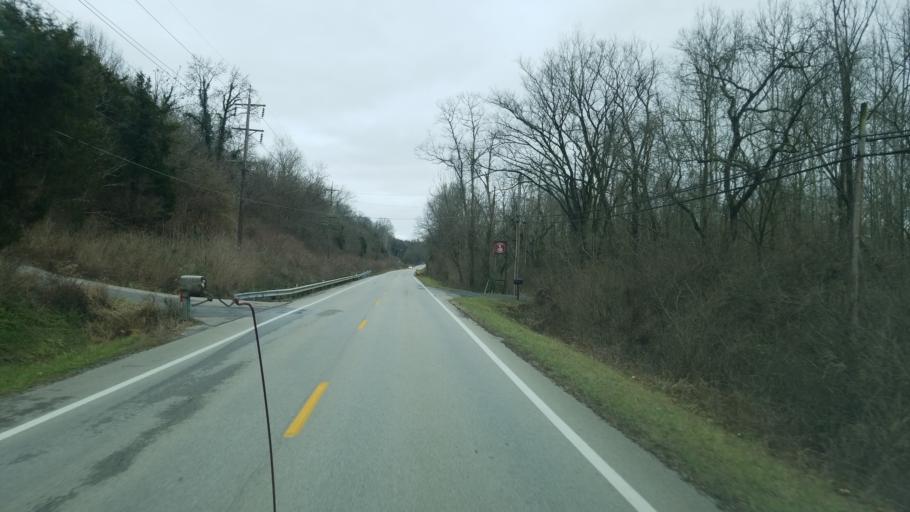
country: US
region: Ohio
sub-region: Clermont County
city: New Richmond
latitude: 38.8829
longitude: -84.2281
